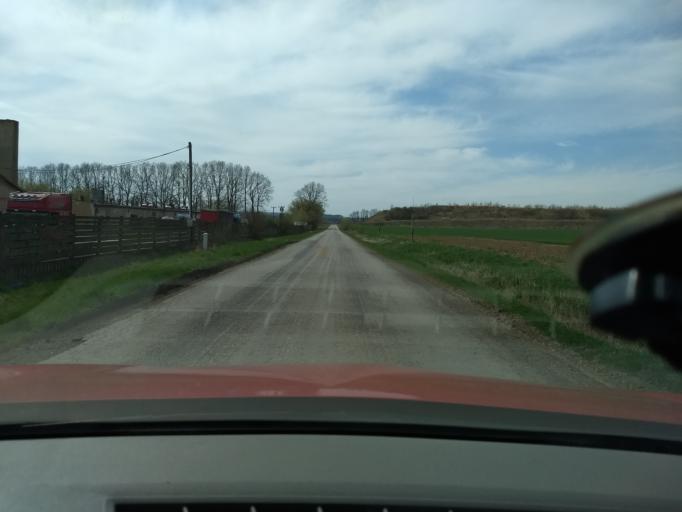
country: CZ
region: Central Bohemia
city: Rudna
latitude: 50.0501
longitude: 14.2059
